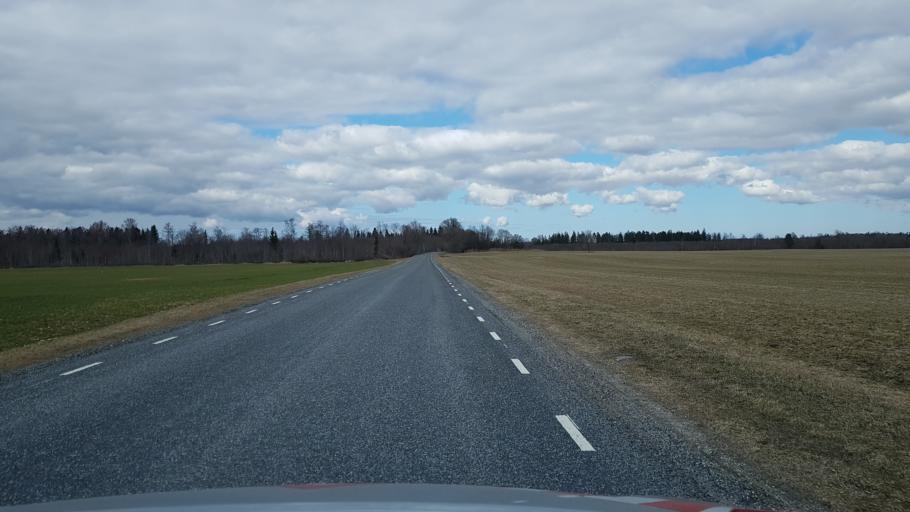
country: EE
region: Laeaene-Virumaa
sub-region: Tamsalu vald
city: Tamsalu
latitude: 59.1801
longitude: 26.1275
